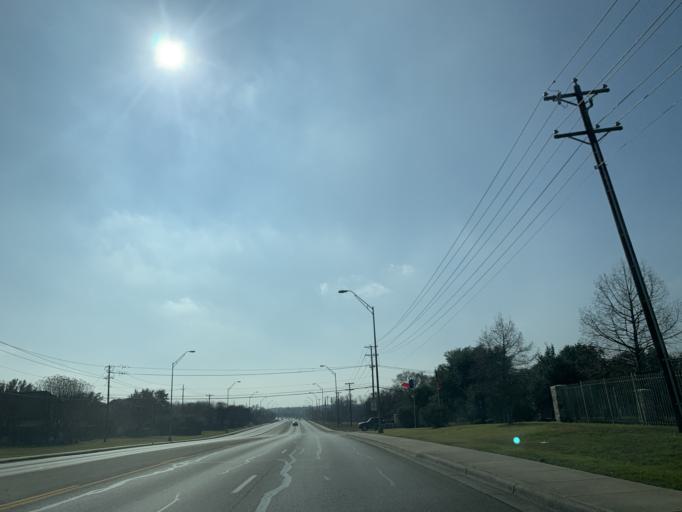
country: US
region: Texas
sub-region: Williamson County
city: Round Rock
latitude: 30.5392
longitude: -97.6513
